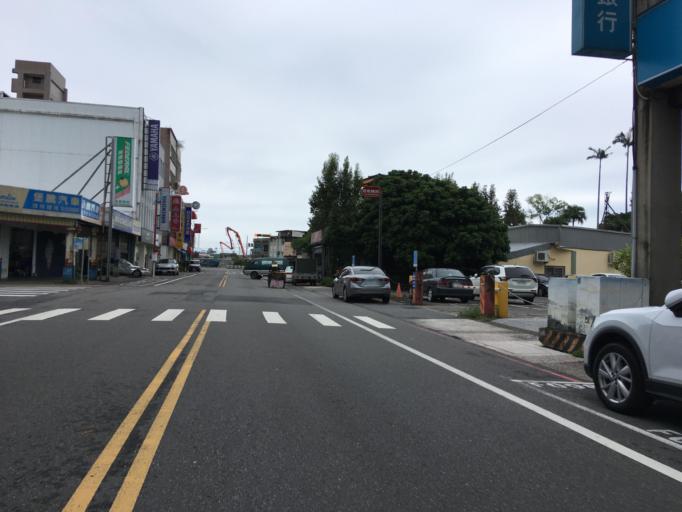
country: TW
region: Taiwan
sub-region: Yilan
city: Yilan
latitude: 24.6846
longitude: 121.7706
